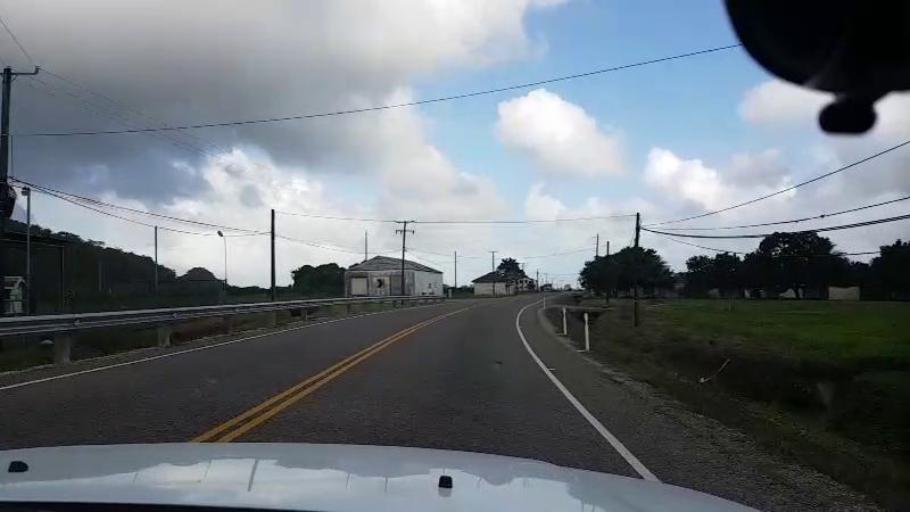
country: BZ
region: Stann Creek
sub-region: Dangriga
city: Dangriga
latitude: 16.9947
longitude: -88.3707
